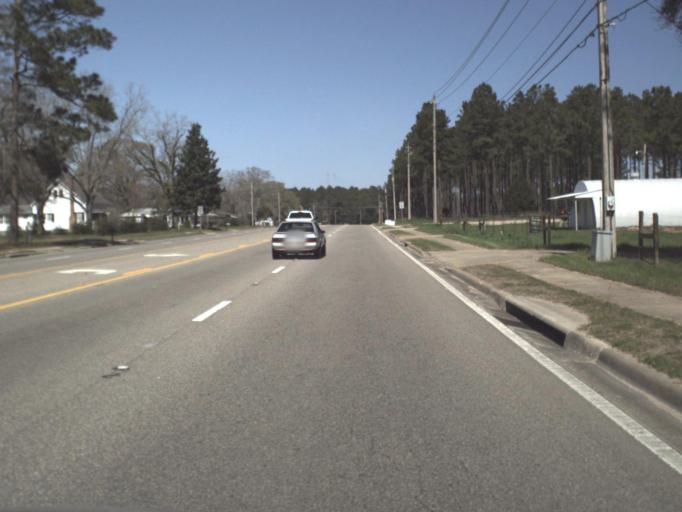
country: US
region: Florida
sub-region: Gadsden County
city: Quincy
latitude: 30.5634
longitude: -84.5924
